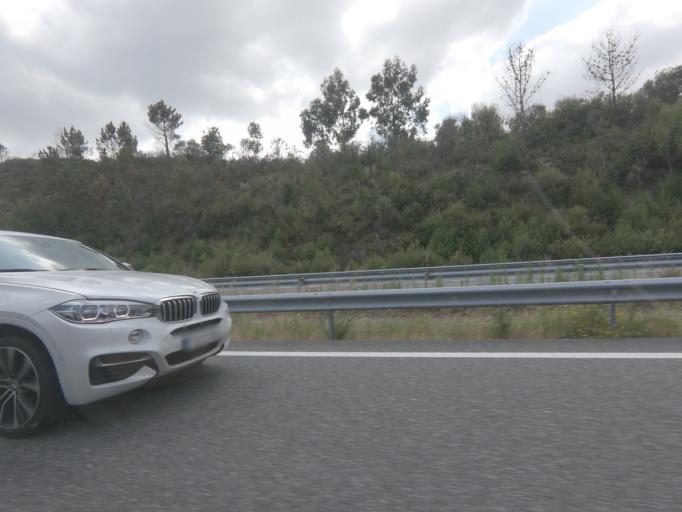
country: ES
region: Galicia
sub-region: Provincia de Ourense
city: Melon
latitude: 42.2820
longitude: -8.2025
